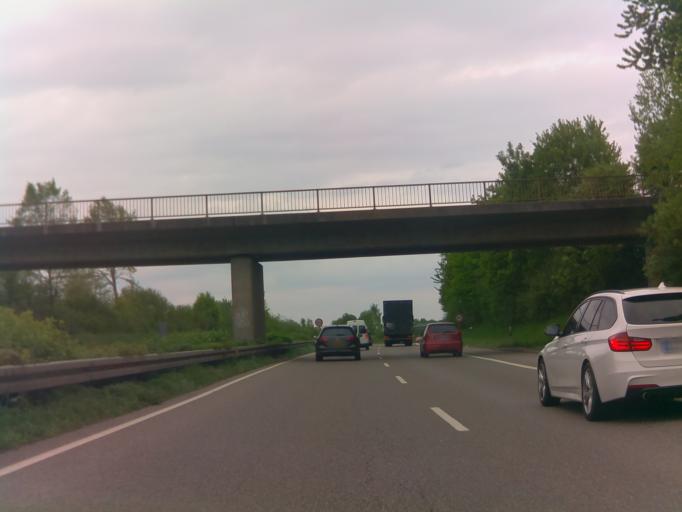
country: DE
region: Baden-Wuerttemberg
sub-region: Regierungsbezirk Stuttgart
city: Magstadt
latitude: 48.6944
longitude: 8.9673
